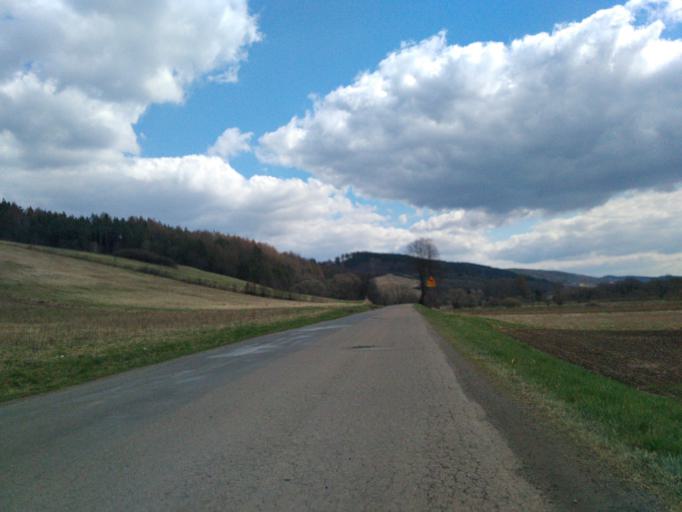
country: PL
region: Subcarpathian Voivodeship
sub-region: Powiat sanocki
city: Tyrawa Woloska
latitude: 49.6053
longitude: 22.3015
